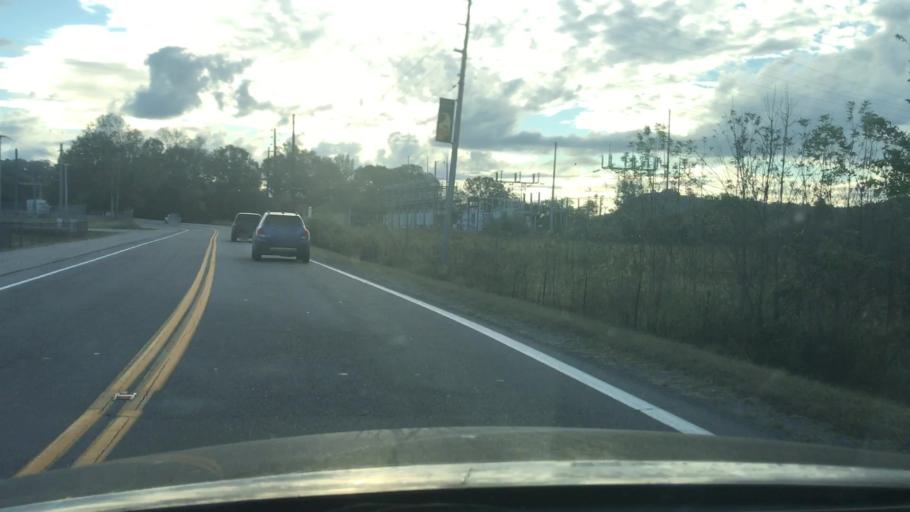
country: US
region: Tennessee
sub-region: Cheatham County
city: Ashland City
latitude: 36.2629
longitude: -87.0655
